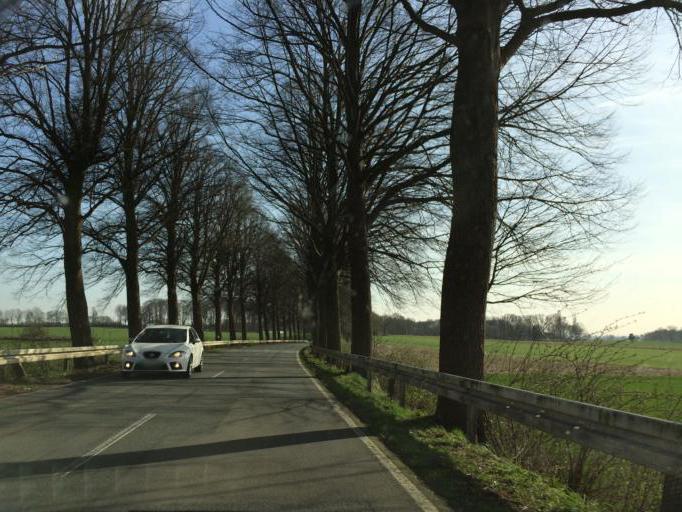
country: DE
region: North Rhine-Westphalia
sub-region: Regierungsbezirk Munster
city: Haltern
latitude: 51.7384
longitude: 7.1080
